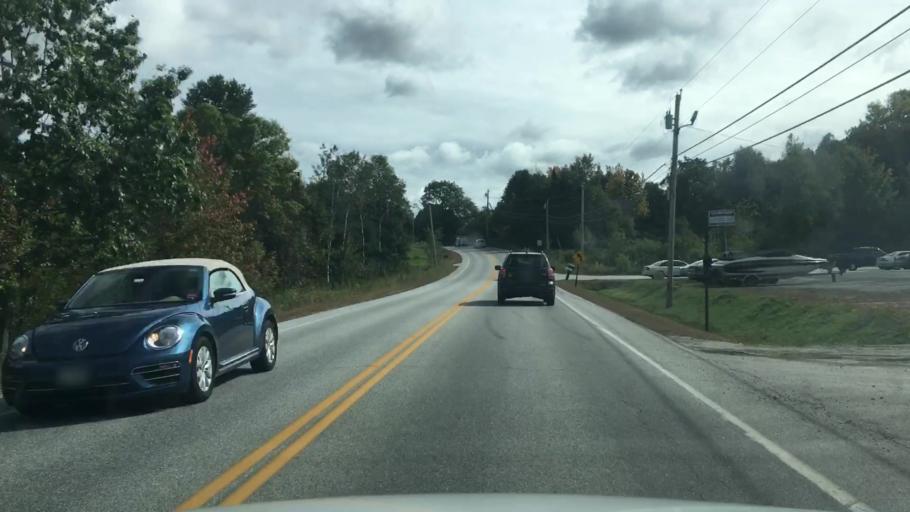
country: US
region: Maine
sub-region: Androscoggin County
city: Lisbon
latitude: 43.9830
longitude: -70.1318
